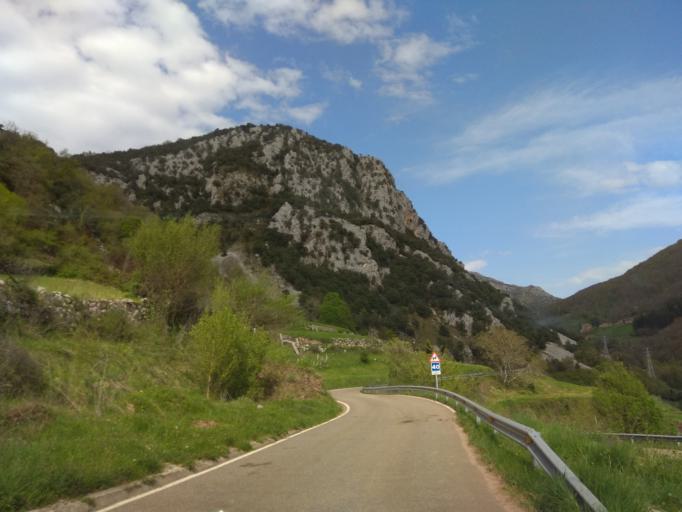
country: ES
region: Cantabria
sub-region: Provincia de Cantabria
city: Tresviso
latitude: 43.2547
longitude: -4.5783
